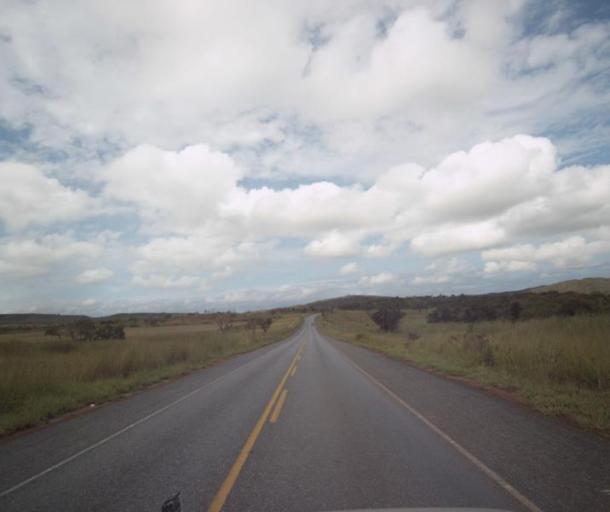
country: BR
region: Goias
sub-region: Pirenopolis
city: Pirenopolis
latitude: -15.6005
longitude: -48.6431
